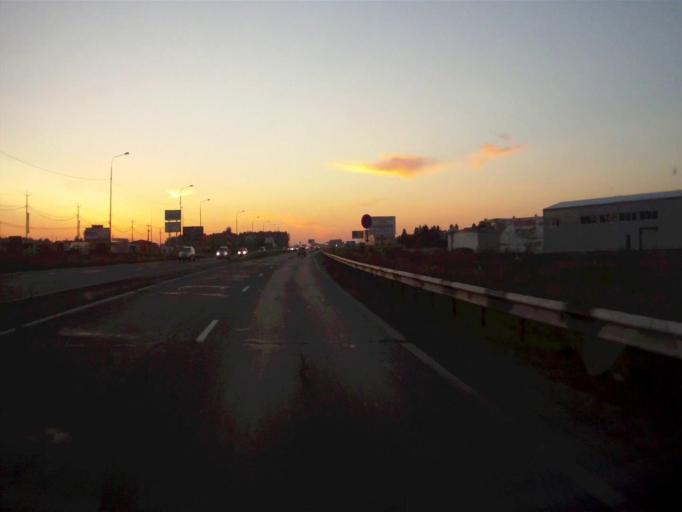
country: RU
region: Chelyabinsk
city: Roshchino
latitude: 55.1803
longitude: 61.2528
